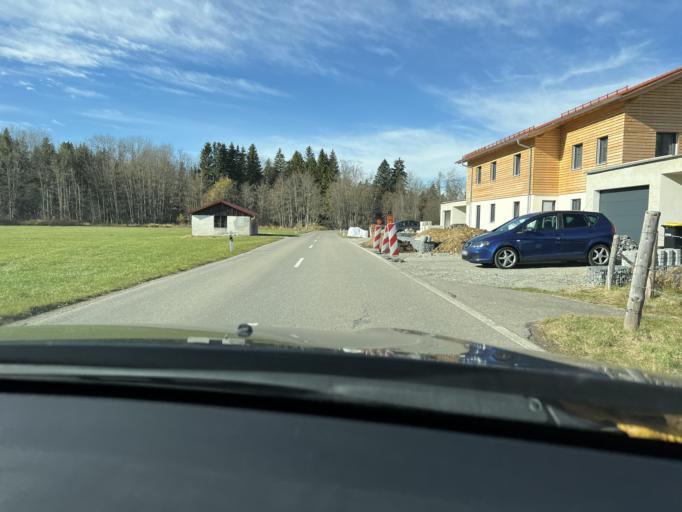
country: DE
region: Baden-Wuerttemberg
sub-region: Tuebingen Region
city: Isny im Allgau
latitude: 47.7092
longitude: 9.9974
